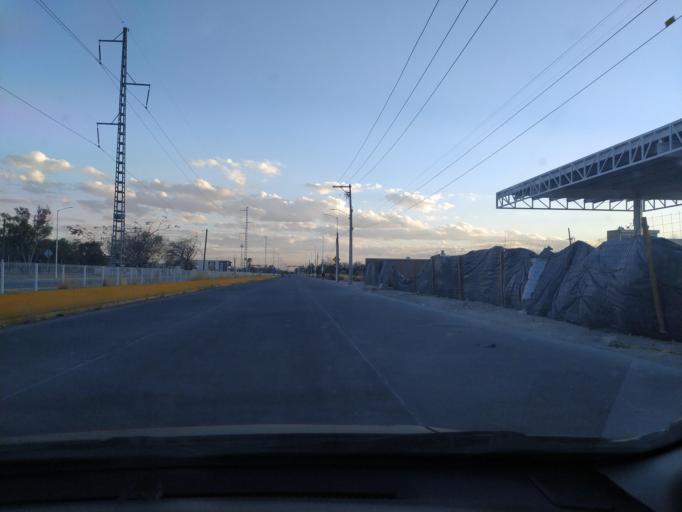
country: LA
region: Oudomxai
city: Muang La
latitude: 21.0166
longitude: 101.8698
